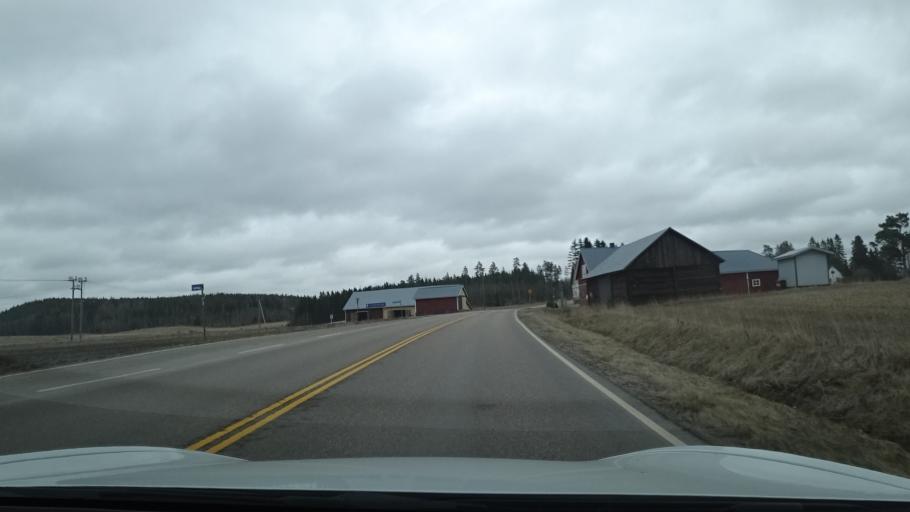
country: FI
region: Paijanne Tavastia
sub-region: Lahti
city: Artjaervi
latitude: 60.7264
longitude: 25.9648
